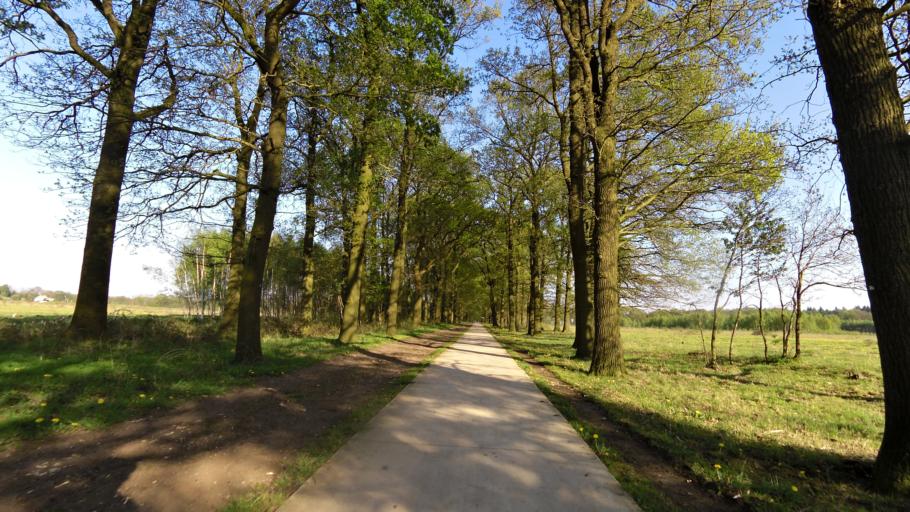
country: NL
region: Gelderland
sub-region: Gemeente Renkum
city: Wolfheze
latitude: 52.0126
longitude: 5.7765
